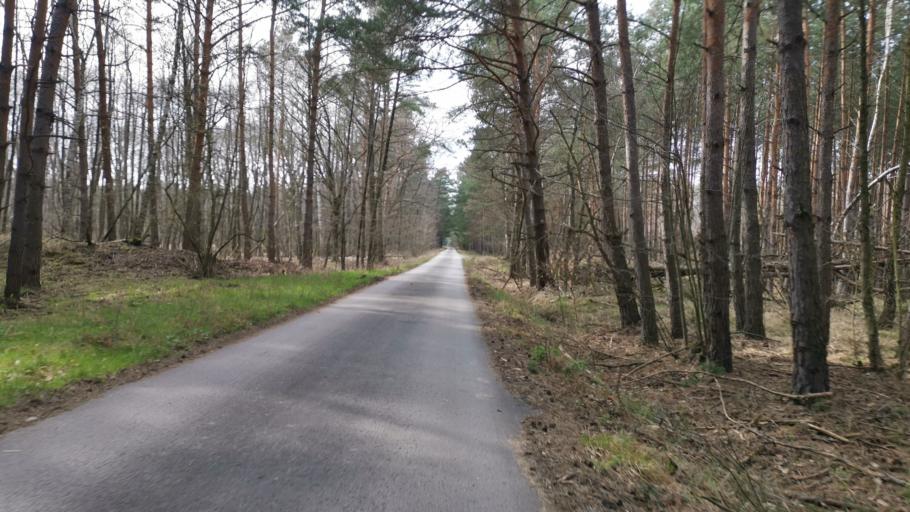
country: SK
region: Trnavsky
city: Gbely
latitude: 48.6883
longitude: 17.0577
